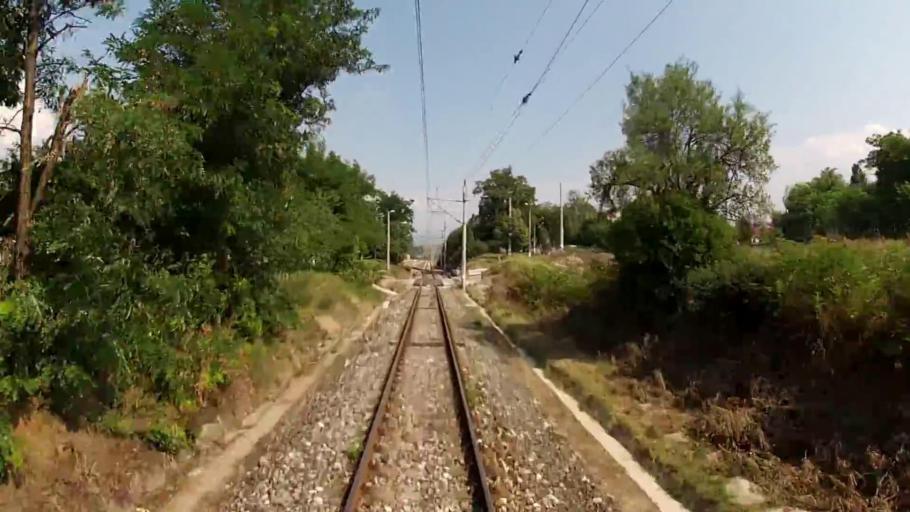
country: BG
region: Blagoevgrad
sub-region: Obshtina Strumyani
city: Strumyani
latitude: 41.6293
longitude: 23.2118
